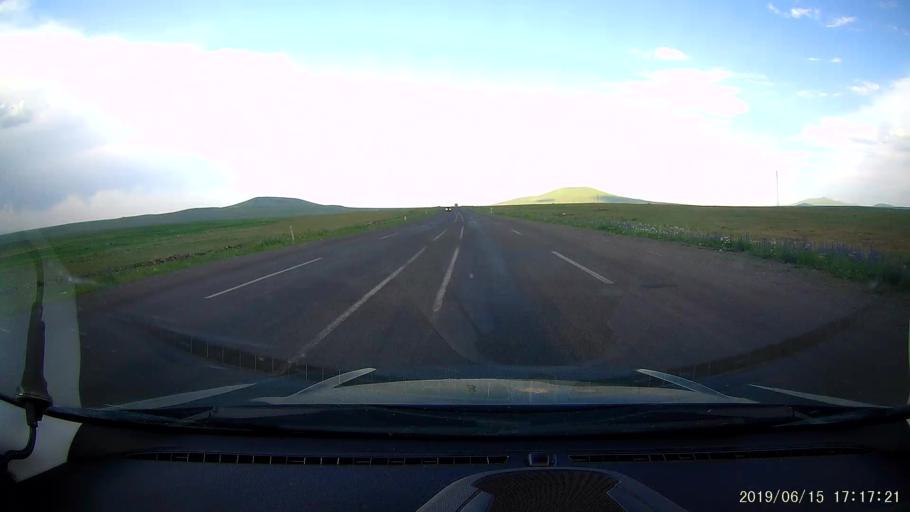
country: TR
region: Kars
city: Kars
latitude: 40.6146
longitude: 43.2369
